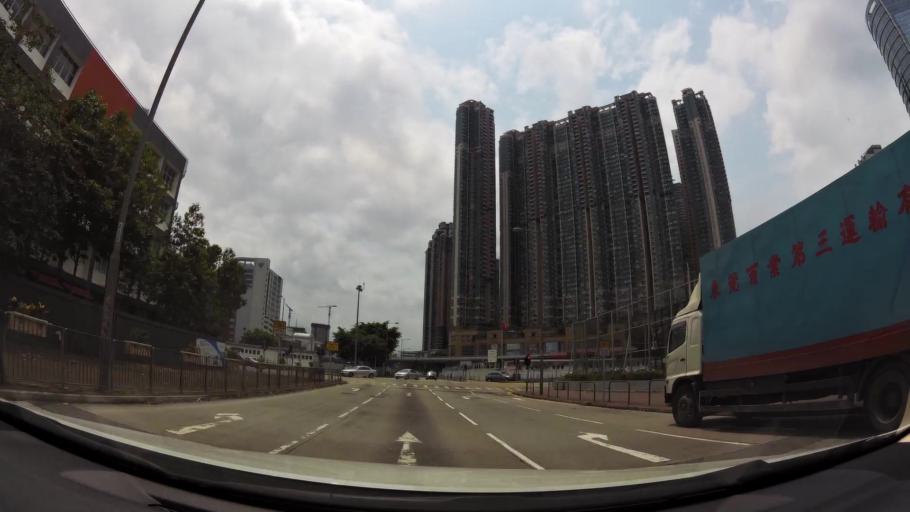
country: HK
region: Sham Shui Po
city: Sham Shui Po
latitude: 22.3358
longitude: 114.1521
